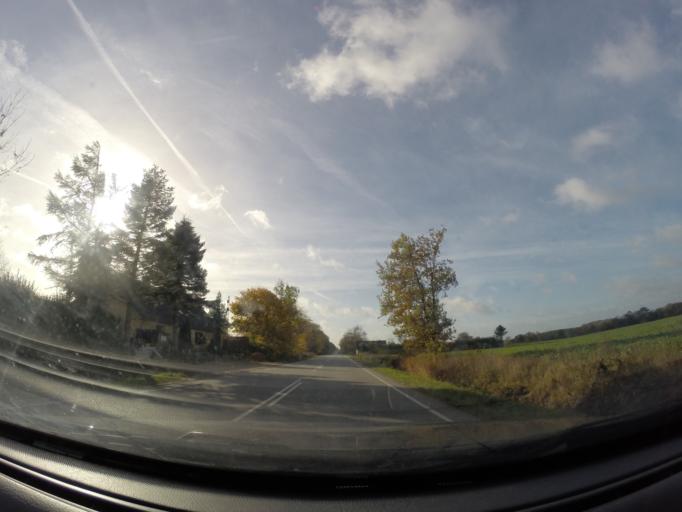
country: DK
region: South Denmark
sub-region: Faaborg-Midtfyn Kommune
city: Ringe
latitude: 55.2016
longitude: 10.5604
